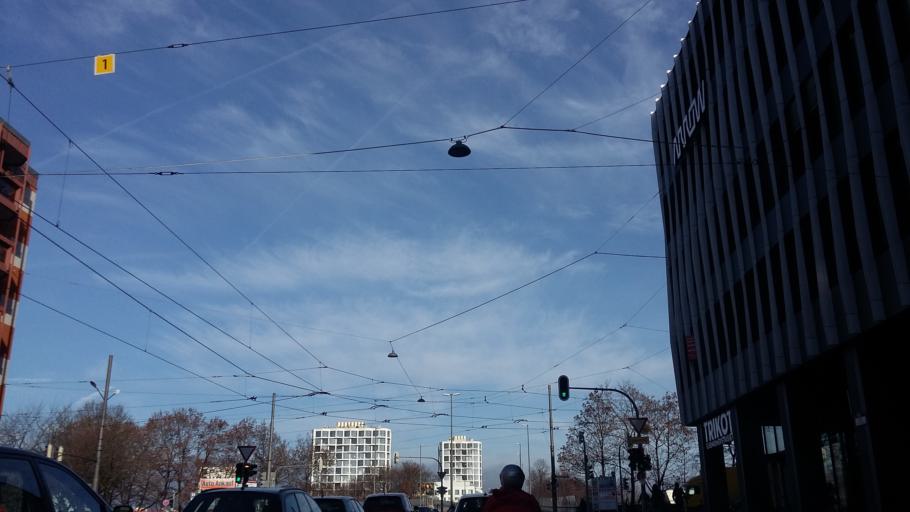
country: DE
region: Bavaria
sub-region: Upper Bavaria
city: Munich
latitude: 48.1408
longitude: 11.5186
